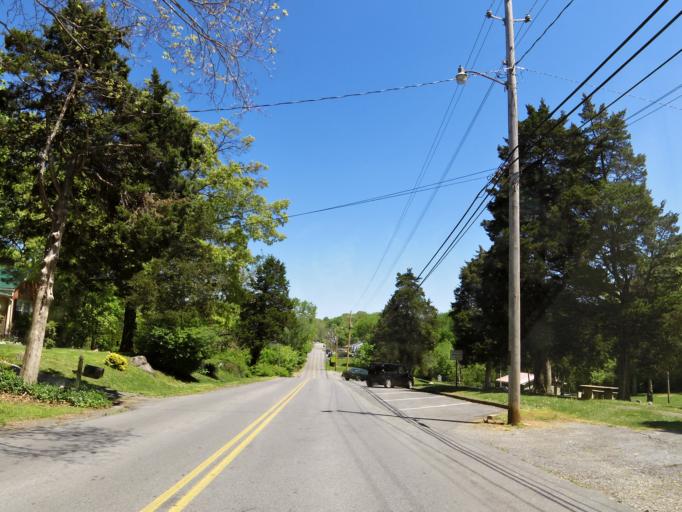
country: US
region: Tennessee
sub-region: Greene County
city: Greeneville
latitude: 36.1545
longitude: -82.8436
